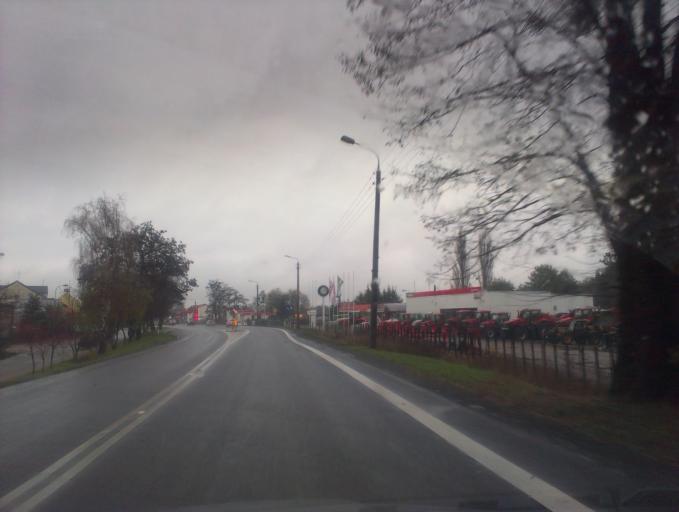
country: PL
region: Greater Poland Voivodeship
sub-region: Powiat obornicki
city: Oborniki
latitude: 52.6365
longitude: 16.8132
